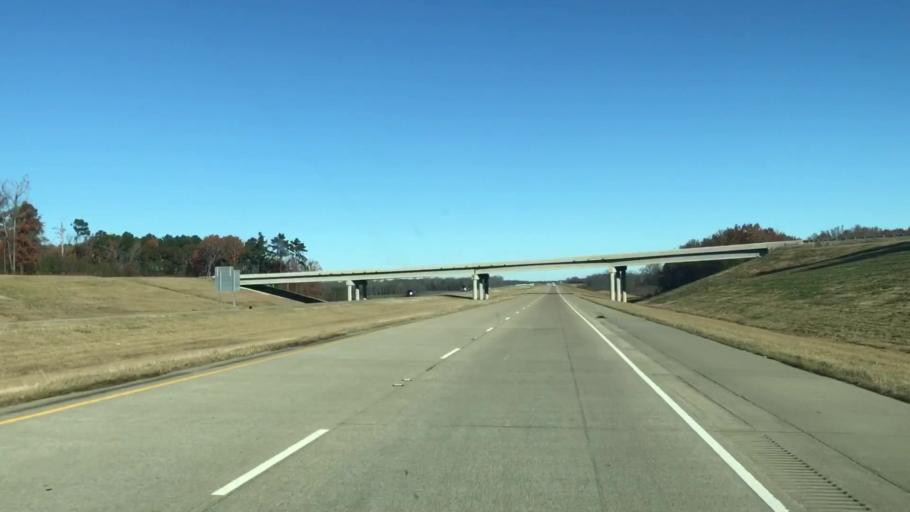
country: US
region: Louisiana
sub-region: Caddo Parish
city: Blanchard
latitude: 32.6145
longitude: -93.8347
